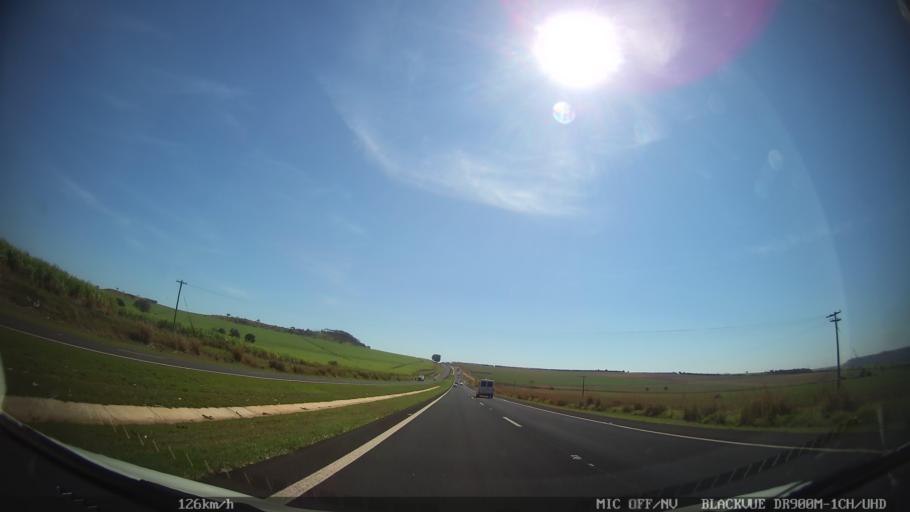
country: BR
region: Sao Paulo
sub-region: Sao Simao
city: Sao Simao
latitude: -21.4405
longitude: -47.6499
